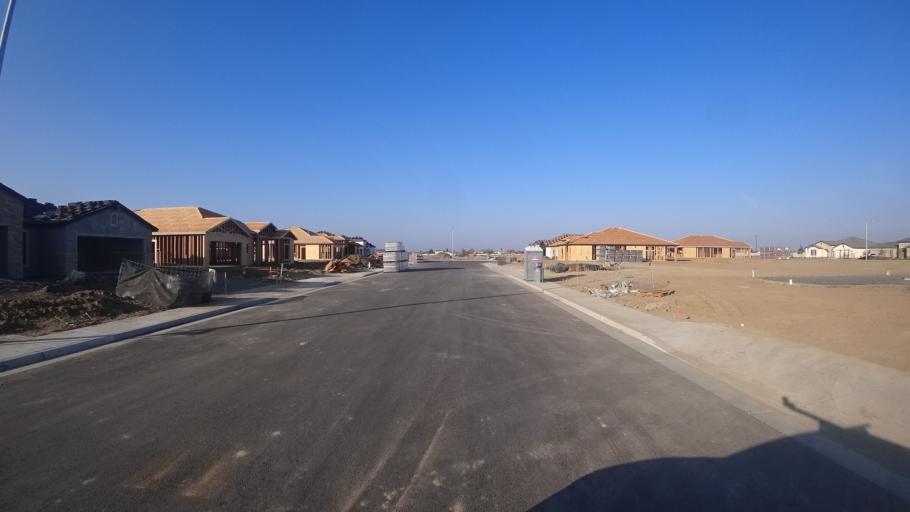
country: US
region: California
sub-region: Kern County
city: Greenacres
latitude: 35.2946
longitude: -119.1133
